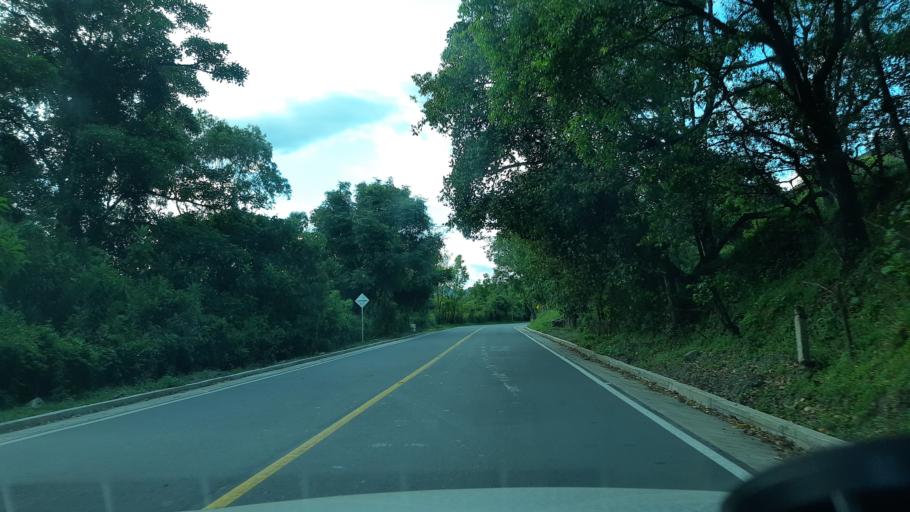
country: CO
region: Boyaca
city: Somondoco
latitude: 4.9922
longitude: -73.3504
